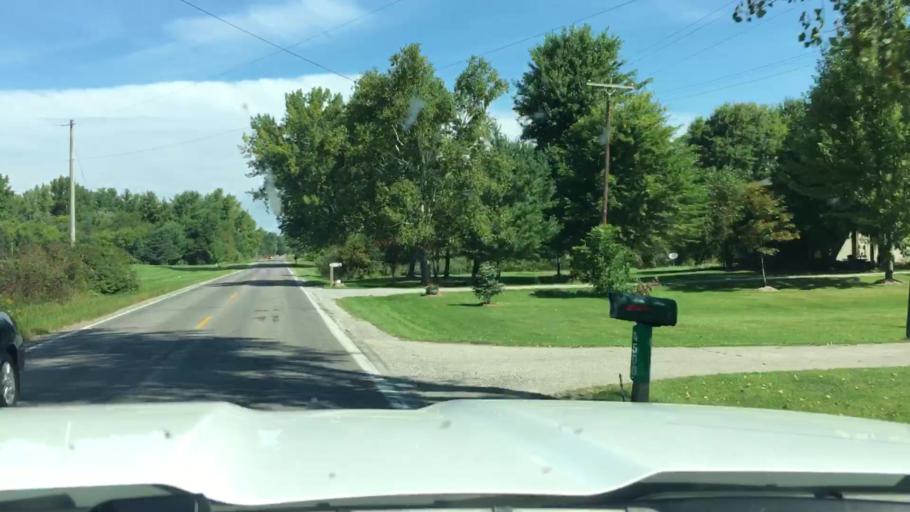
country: US
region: Michigan
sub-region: Saginaw County
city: Hemlock
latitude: 43.4737
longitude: -84.2303
